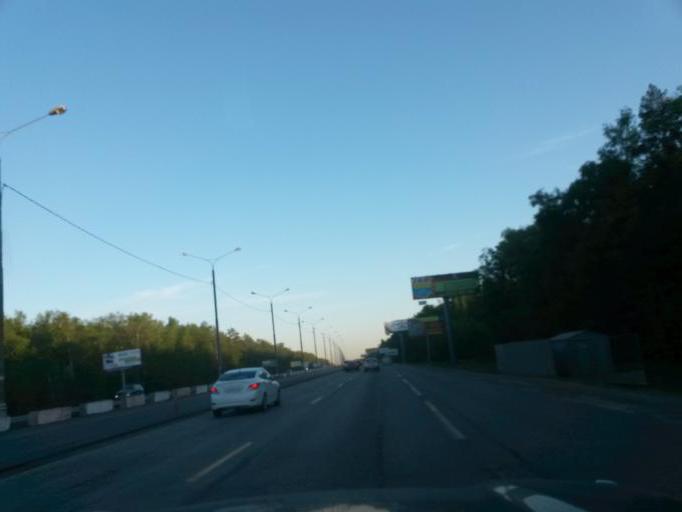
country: RU
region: Moskovskaya
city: Shcherbinka
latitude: 55.5164
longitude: 37.6083
